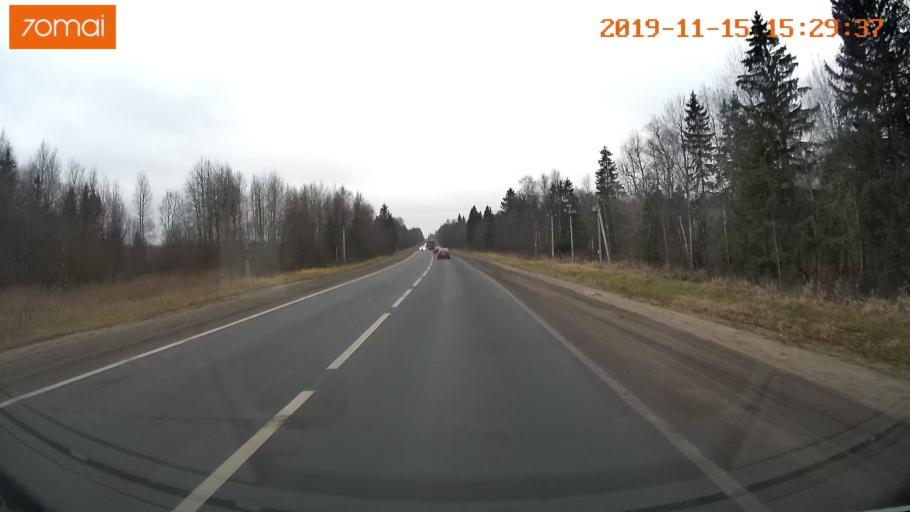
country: RU
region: Jaroslavl
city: Danilov
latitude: 58.1188
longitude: 40.1182
